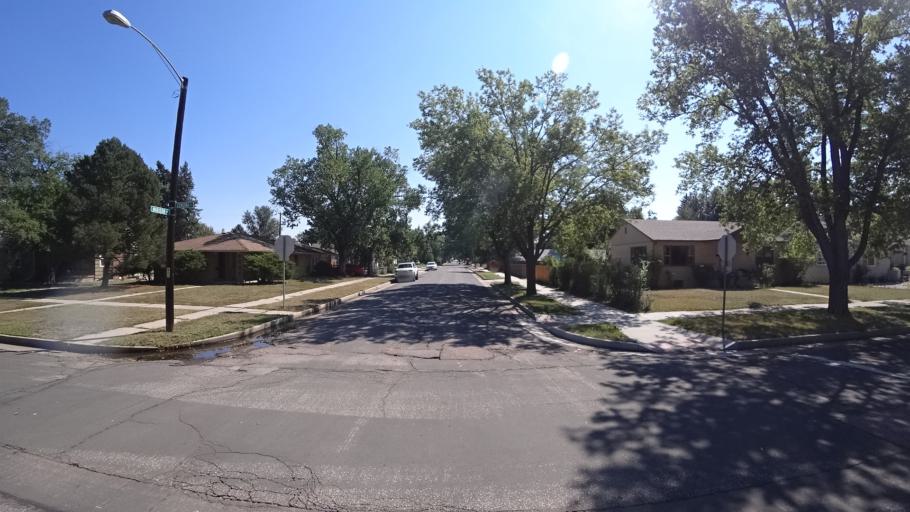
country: US
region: Colorado
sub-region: El Paso County
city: Colorado Springs
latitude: 38.8642
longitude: -104.8147
